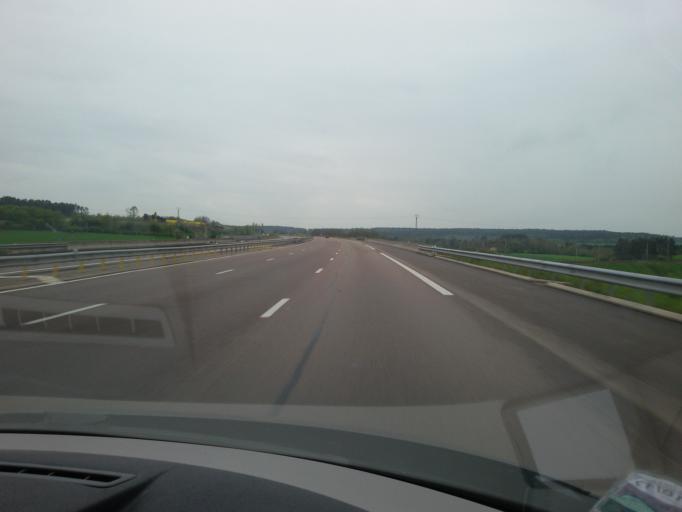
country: FR
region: Bourgogne
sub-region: Departement de la Cote-d'Or
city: Selongey
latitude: 47.5755
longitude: 5.2094
